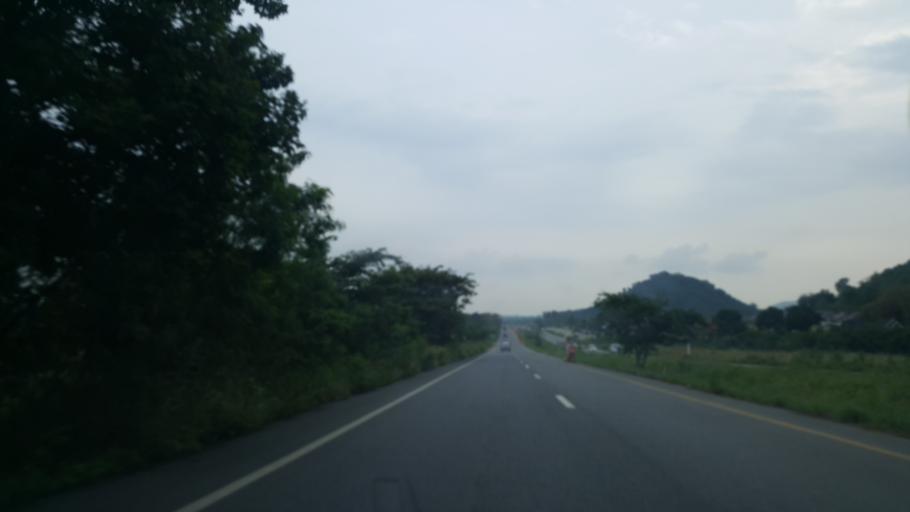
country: TH
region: Rayong
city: Ban Chang
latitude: 12.7502
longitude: 100.9914
